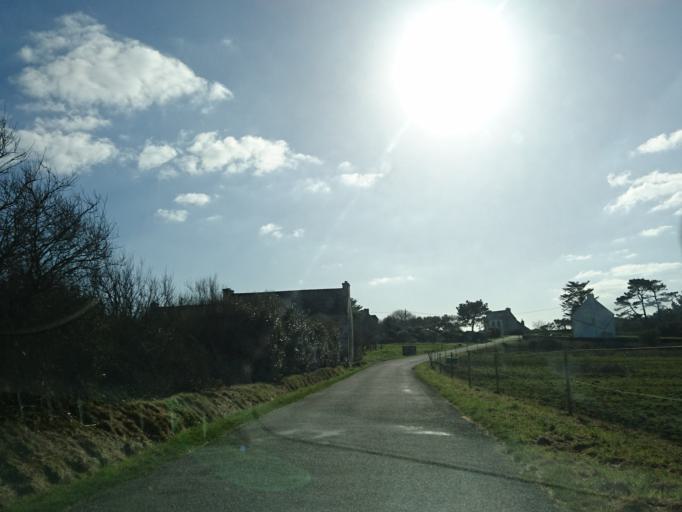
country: FR
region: Brittany
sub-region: Departement du Finistere
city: Roscanvel
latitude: 48.3259
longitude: -4.5698
